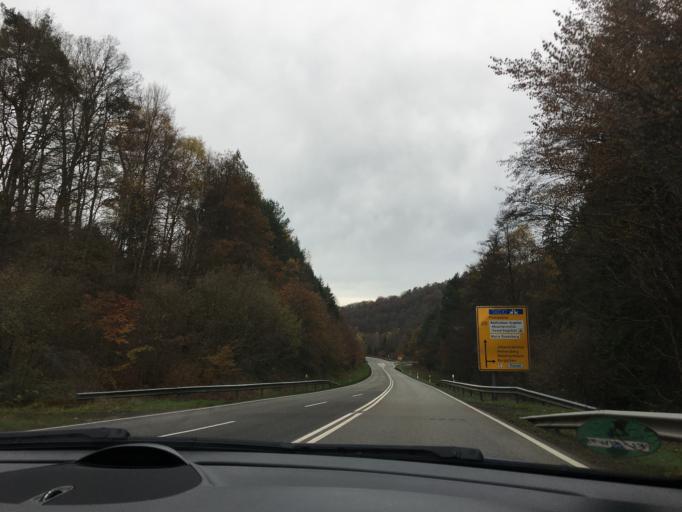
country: DE
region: Rheinland-Pfalz
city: Steinalben
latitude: 49.3049
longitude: 7.6620
